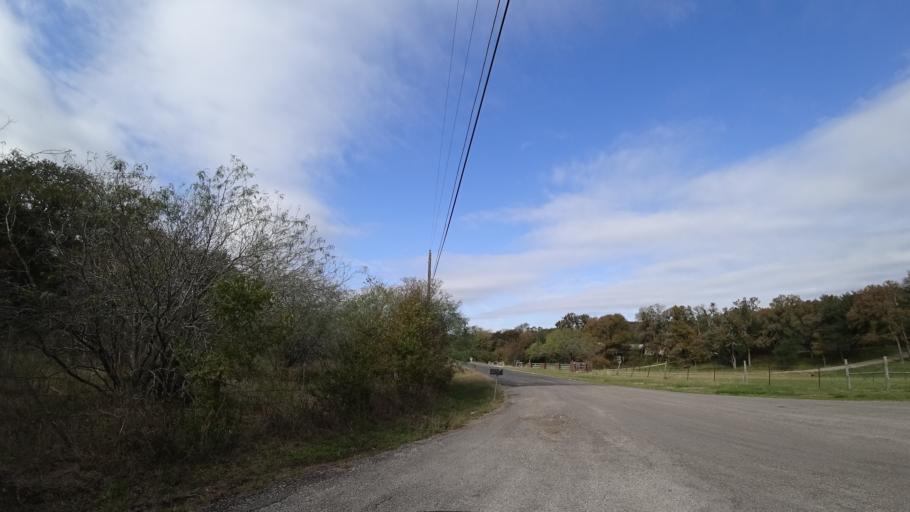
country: US
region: Texas
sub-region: Travis County
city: Manchaca
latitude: 30.1296
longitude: -97.8534
